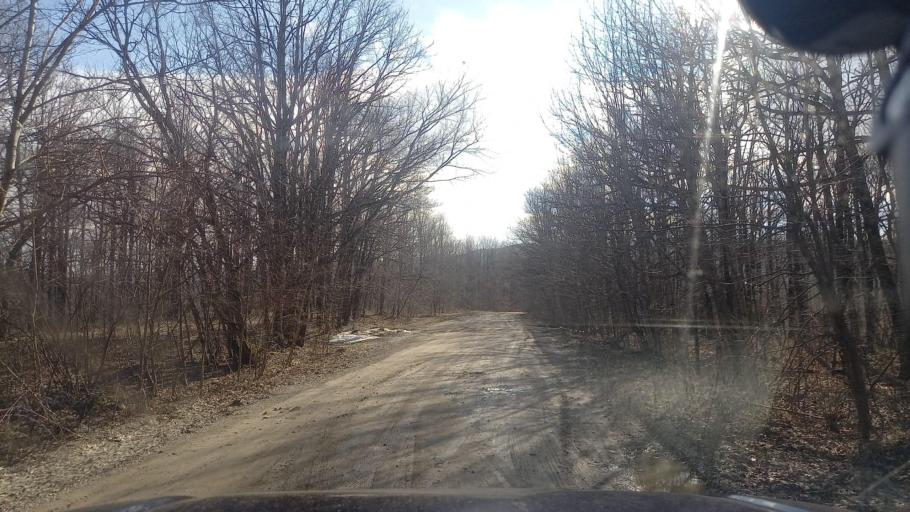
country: RU
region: Krasnodarskiy
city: Goryachiy Klyuch
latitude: 44.6911
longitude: 38.9842
